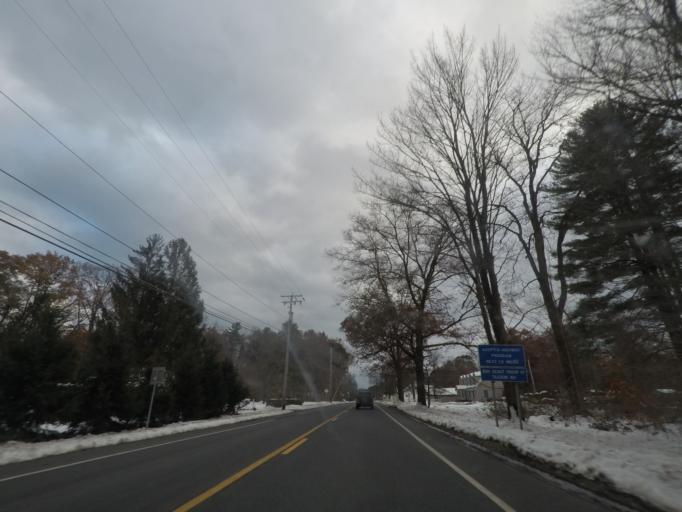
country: US
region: New York
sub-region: Ulster County
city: Tillson
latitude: 41.8336
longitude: -74.0697
